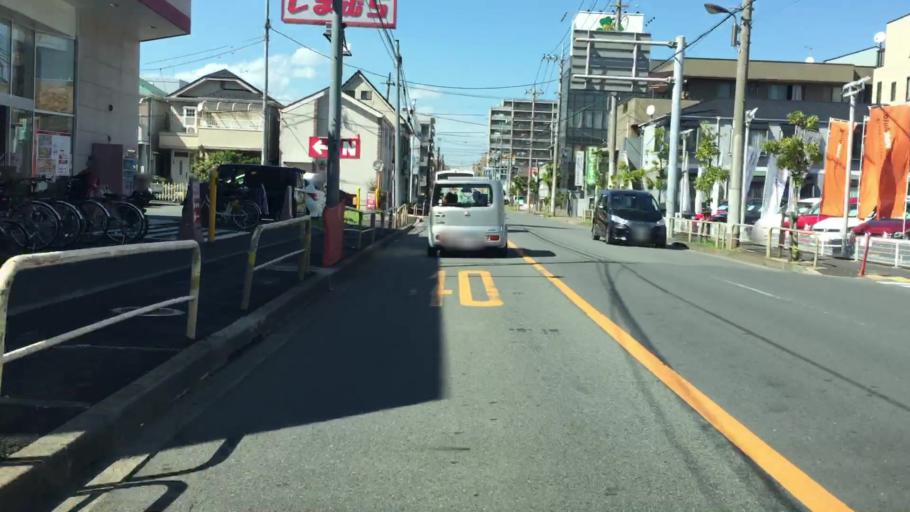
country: JP
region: Saitama
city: Yashio-shi
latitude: 35.7787
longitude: 139.8264
